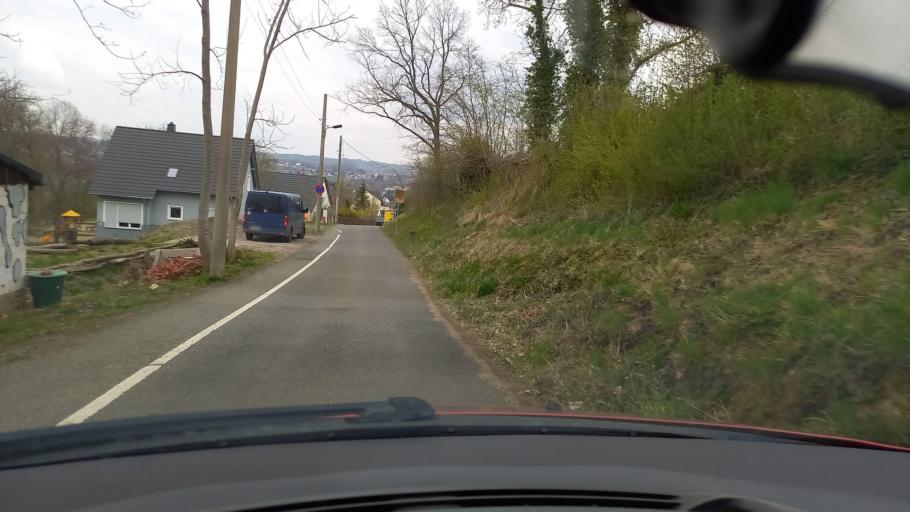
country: DE
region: Saxony
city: Wilkau-Hasslau
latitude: 50.6794
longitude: 12.4926
